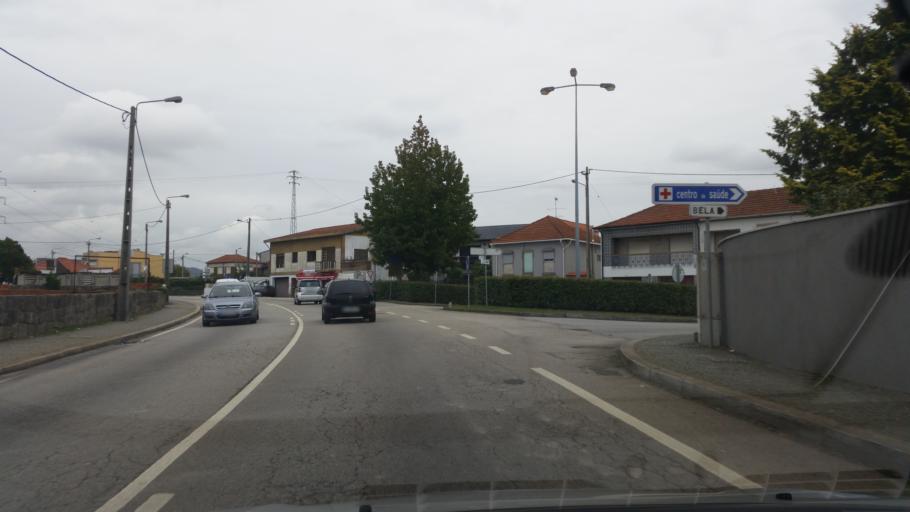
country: PT
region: Porto
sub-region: Valongo
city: Ermesinde
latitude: 41.2325
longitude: -8.5449
